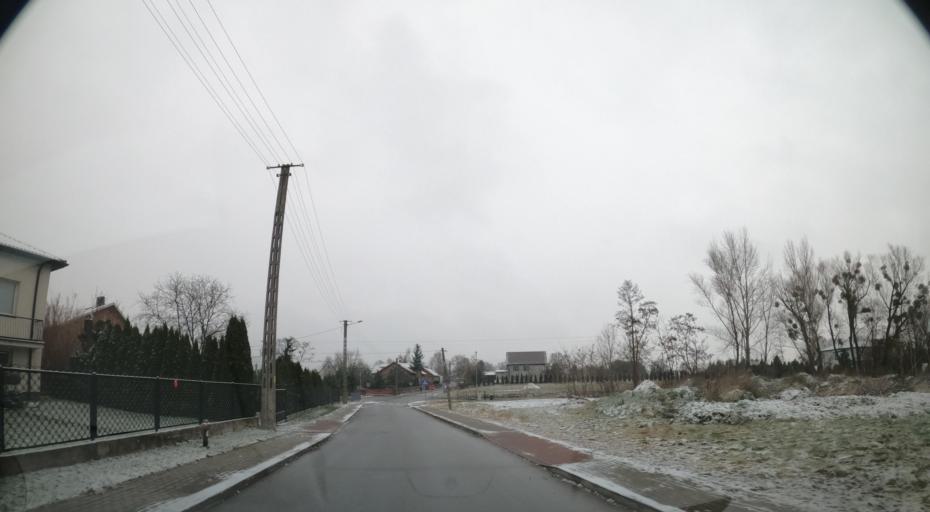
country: PL
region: Masovian Voivodeship
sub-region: Powiat plocki
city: Wyszogrod
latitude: 52.3868
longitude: 20.1859
